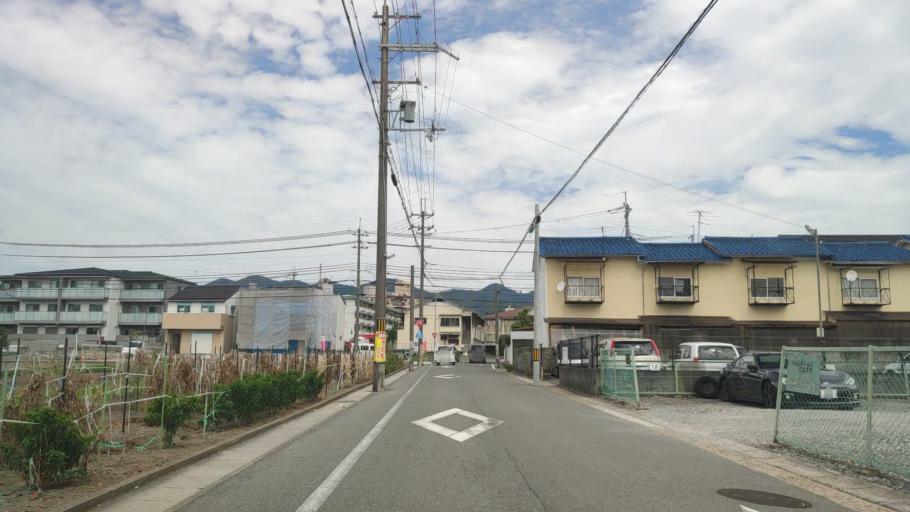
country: JP
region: Kyoto
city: Kyoto
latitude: 35.0186
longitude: 135.7026
